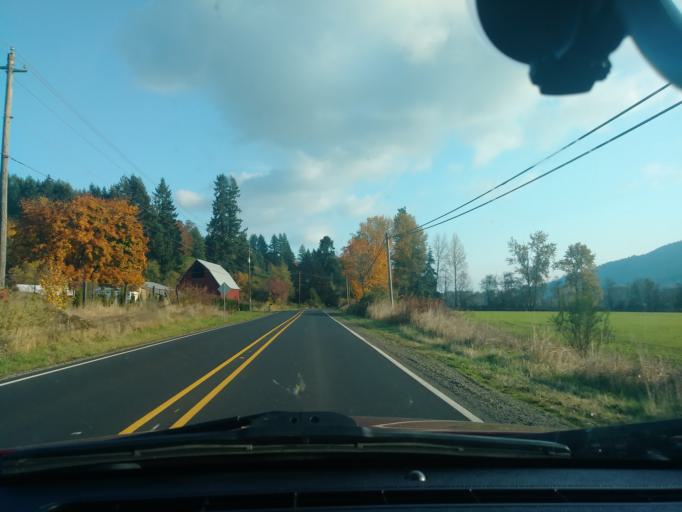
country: US
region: Oregon
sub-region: Washington County
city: Banks
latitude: 45.5691
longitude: -123.1980
